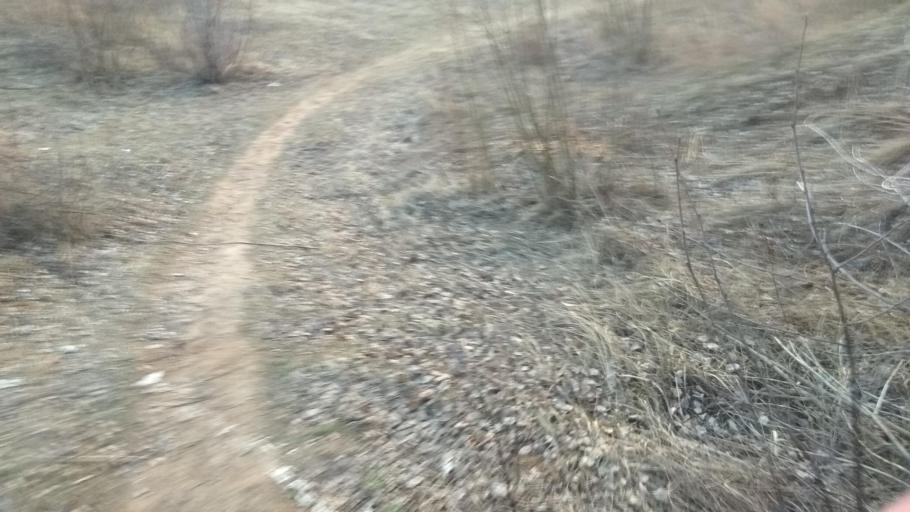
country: RU
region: Moscow
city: Zagor'ye
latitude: 55.5624
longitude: 37.6766
